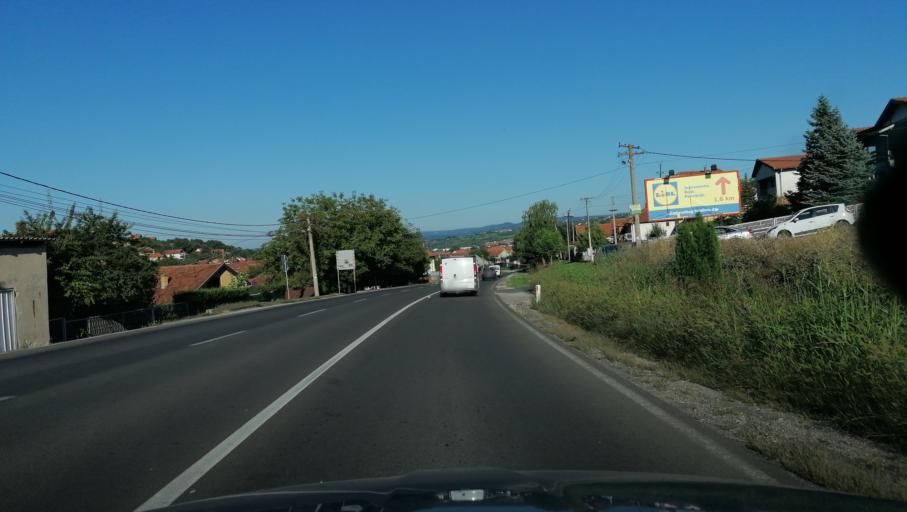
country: RS
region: Central Serbia
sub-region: Sumadijski Okrug
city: Kragujevac
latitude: 43.9922
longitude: 20.8615
